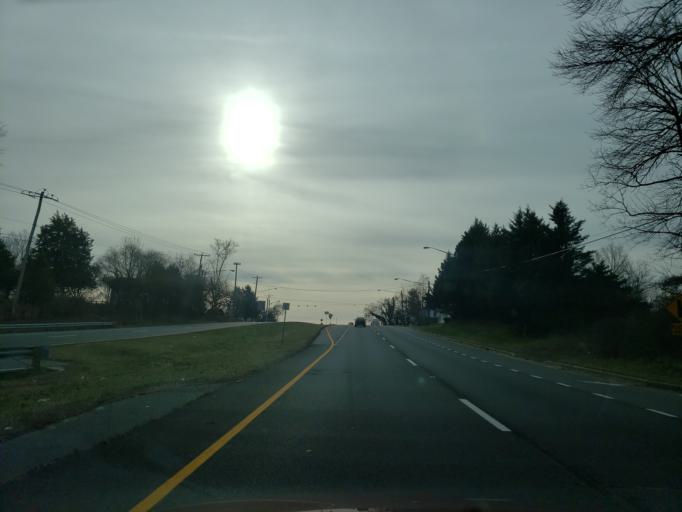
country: US
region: Delaware
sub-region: New Castle County
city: Townsend
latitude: 39.3723
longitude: -75.6613
